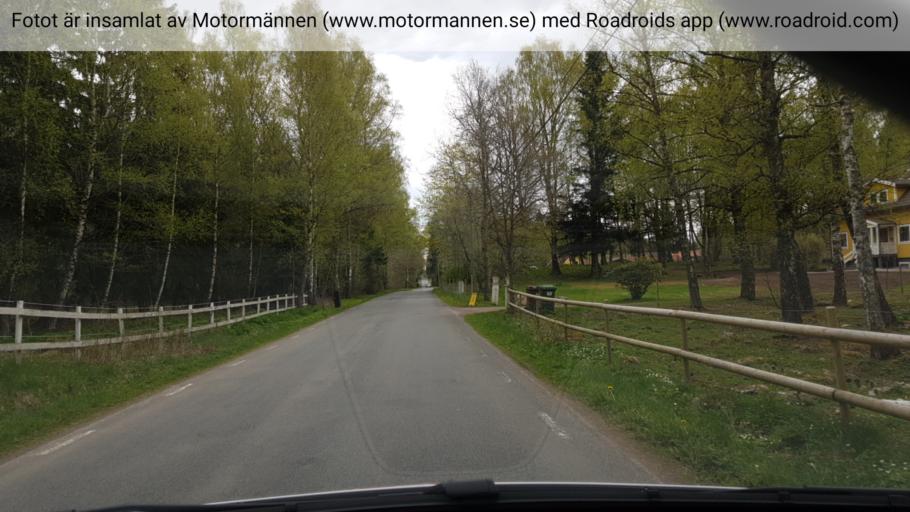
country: SE
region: Vaestra Goetaland
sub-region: Skara Kommun
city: Skara
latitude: 58.3671
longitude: 13.4857
